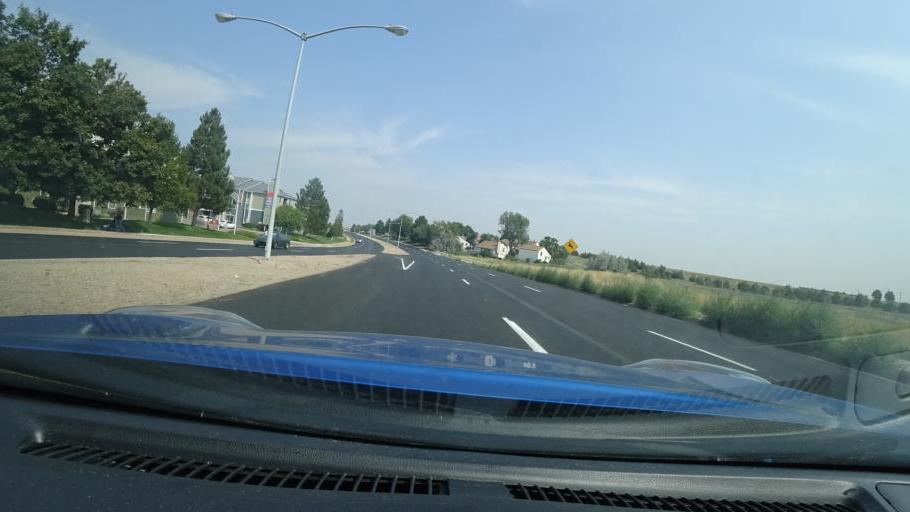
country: US
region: Colorado
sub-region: Adams County
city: Aurora
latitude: 39.6986
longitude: -104.7722
